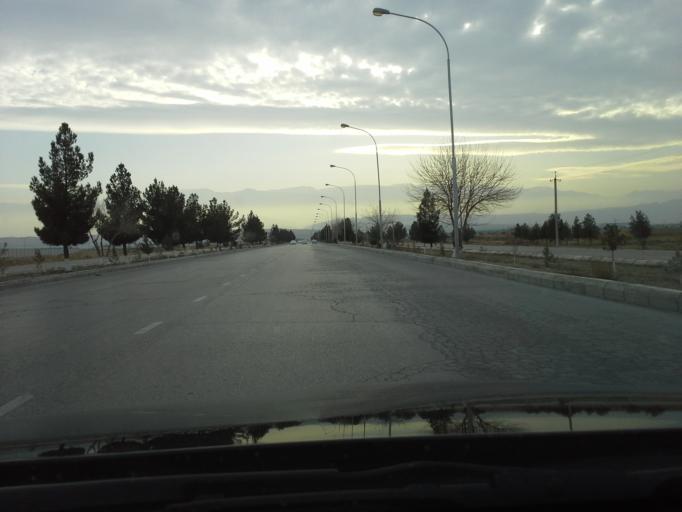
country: TM
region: Ahal
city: Ashgabat
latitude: 38.0066
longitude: 58.3338
